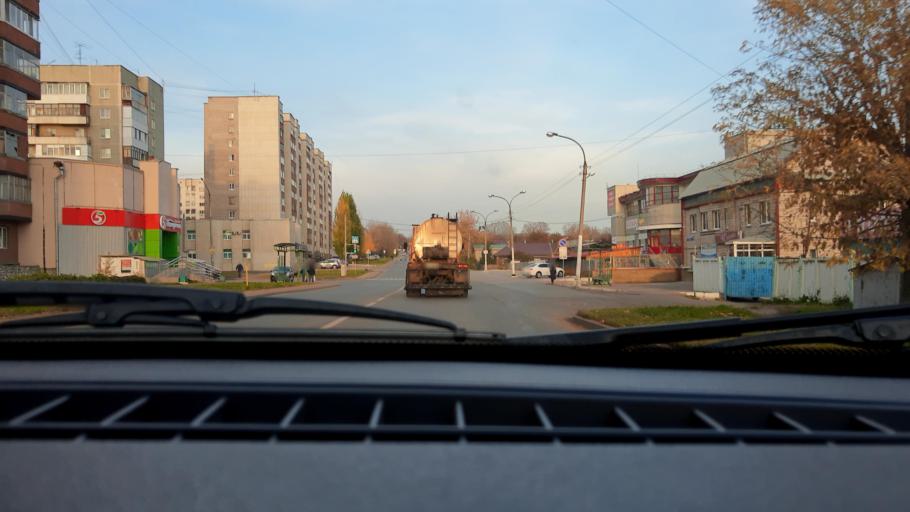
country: RU
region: Bashkortostan
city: Ufa
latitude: 54.8200
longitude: 56.1212
